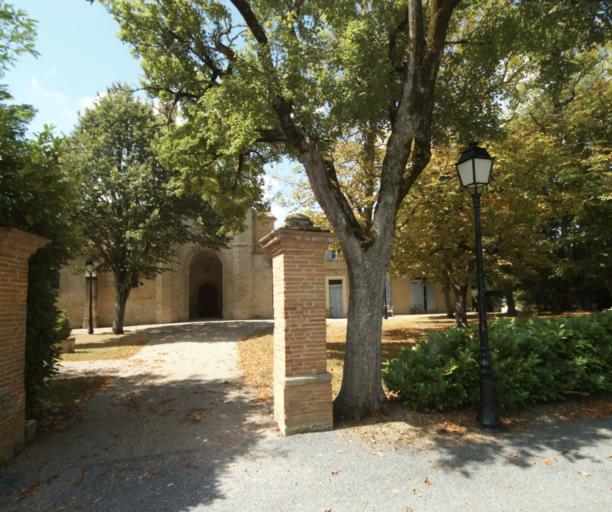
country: FR
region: Midi-Pyrenees
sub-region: Departement de la Haute-Garonne
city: Auriac-sur-Vendinelle
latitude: 43.4637
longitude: 1.7944
